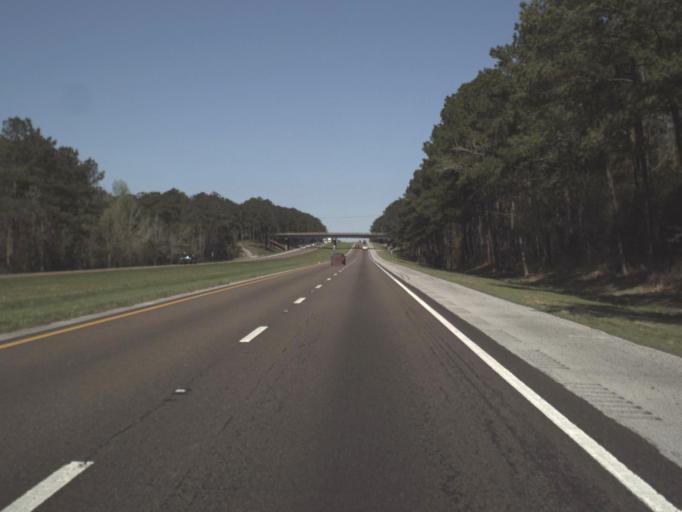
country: US
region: Florida
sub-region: Walton County
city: DeFuniak Springs
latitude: 30.7036
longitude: -86.1593
